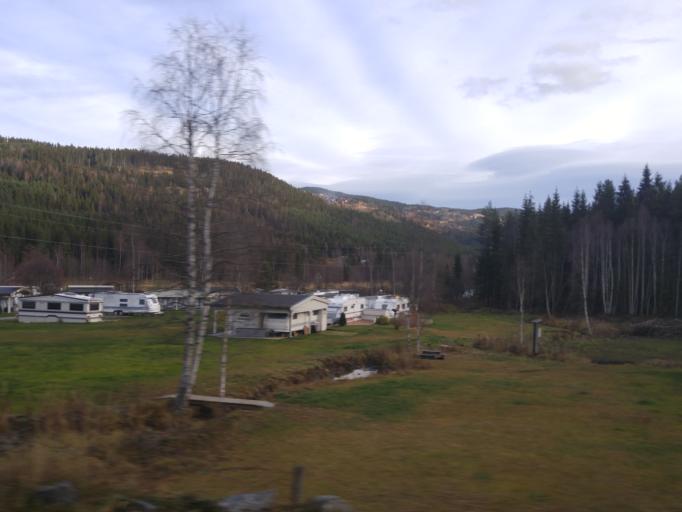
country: NO
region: Oppland
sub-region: Nord-Aurdal
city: Fagernes
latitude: 61.0330
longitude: 9.1760
